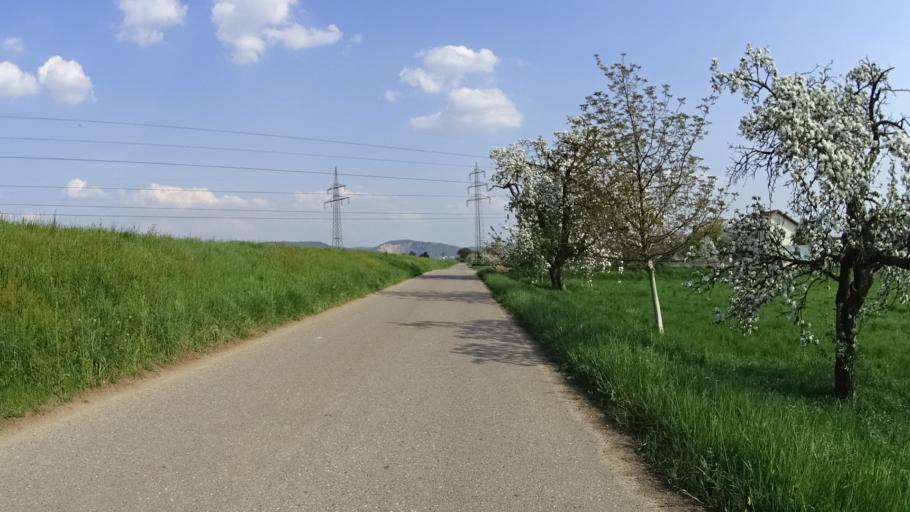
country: DE
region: Baden-Wuerttemberg
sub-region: Karlsruhe Region
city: Hemsbach
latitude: 49.5823
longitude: 8.6139
